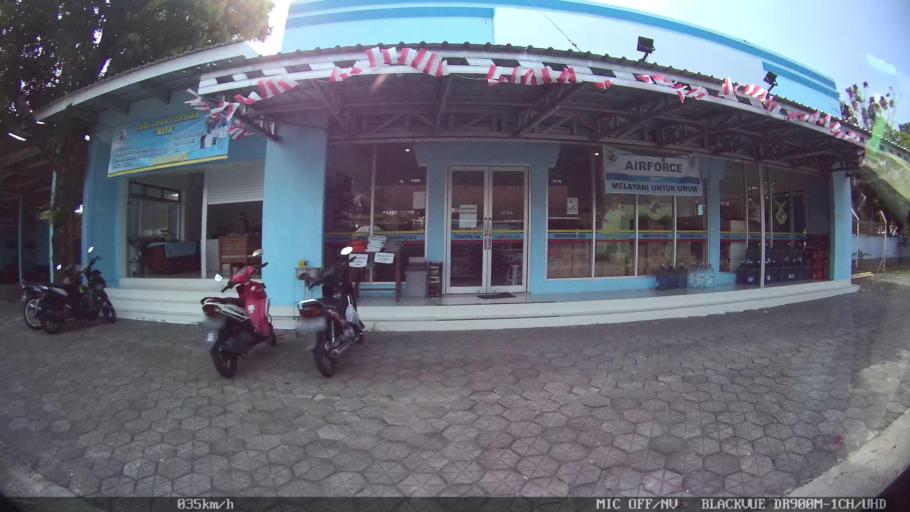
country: ID
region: Daerah Istimewa Yogyakarta
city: Depok
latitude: -7.8038
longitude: 110.4333
